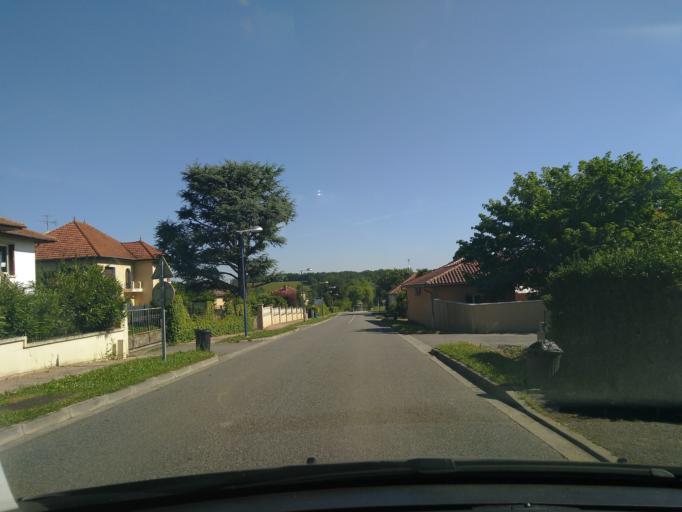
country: FR
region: Midi-Pyrenees
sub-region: Departement du Gers
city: Aubiet
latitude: 43.5261
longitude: 0.7637
